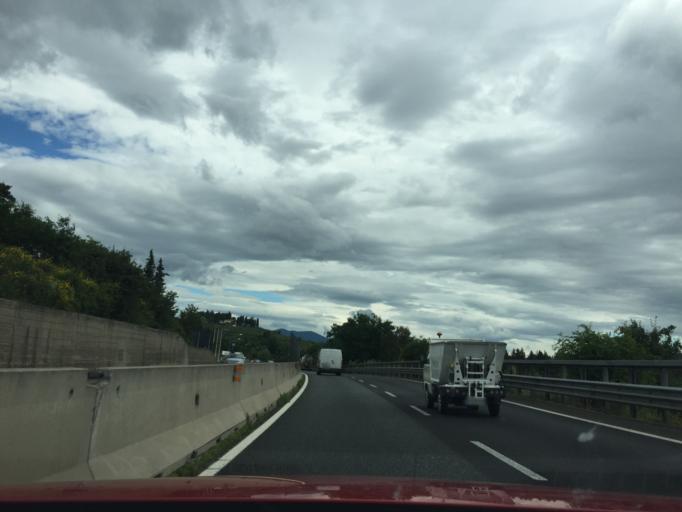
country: IT
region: Tuscany
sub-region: Province of Florence
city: Quattro Strade
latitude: 43.7338
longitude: 11.1051
